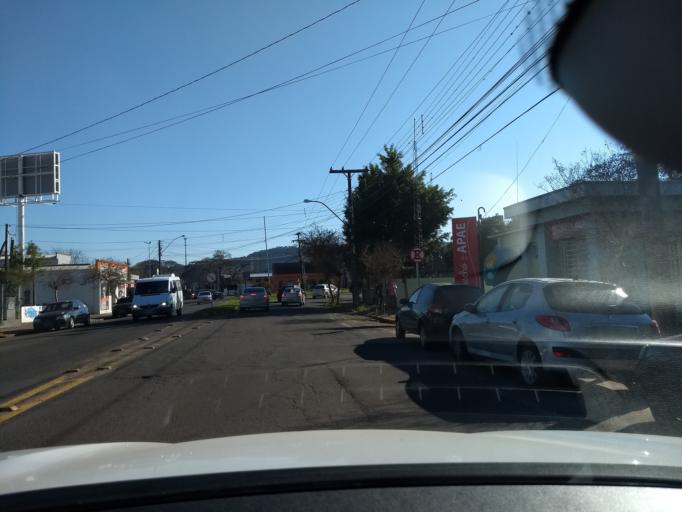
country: BR
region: Rio Grande do Sul
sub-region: Santa Cruz Do Sul
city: Santa Cruz do Sul
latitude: -29.7089
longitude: -52.4356
